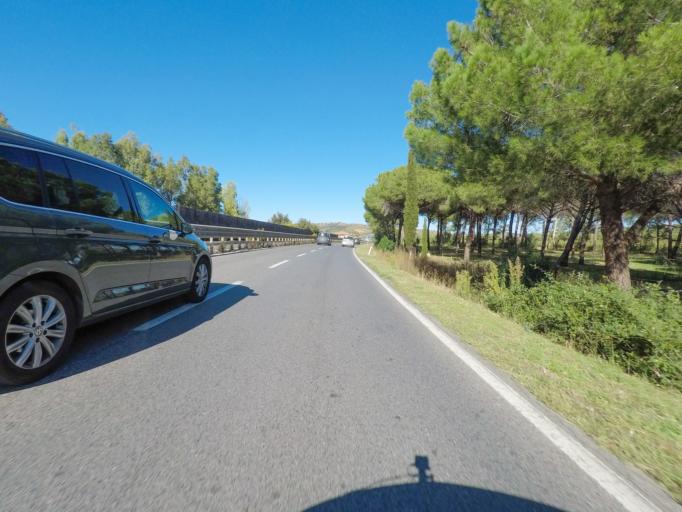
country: IT
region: Tuscany
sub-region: Provincia di Grosseto
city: Grosseto
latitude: 42.7046
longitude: 11.1380
